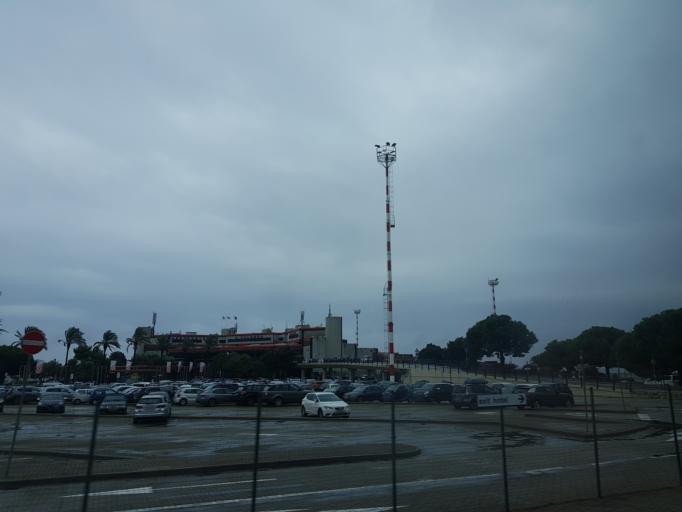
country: IT
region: Liguria
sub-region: Provincia di Genova
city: San Teodoro
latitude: 44.4167
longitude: 8.8519
